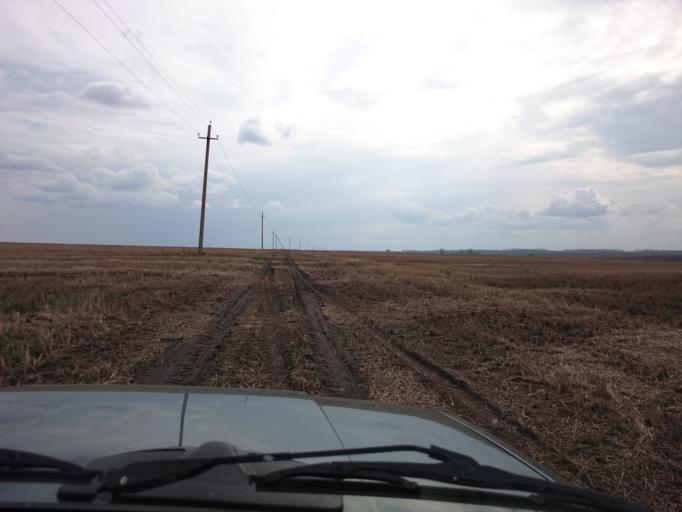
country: RU
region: Mordoviya
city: Kadoshkino
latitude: 54.0251
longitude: 44.4763
